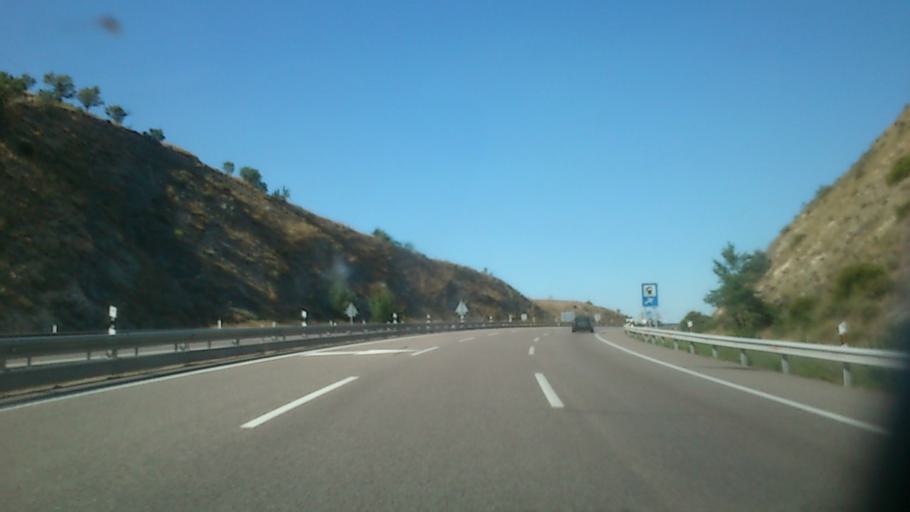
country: ES
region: Aragon
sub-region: Provincia de Zaragoza
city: Paracuellos de la Ribera
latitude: 41.4115
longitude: -1.5266
